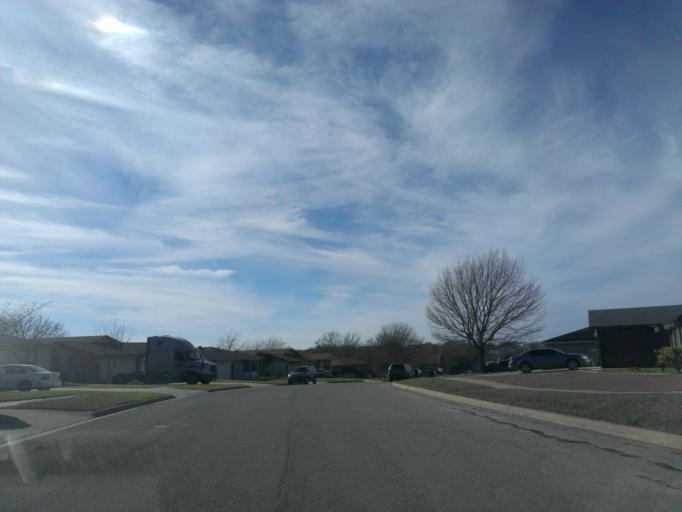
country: US
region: Texas
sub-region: Bell County
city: Killeen
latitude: 31.1383
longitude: -97.6896
